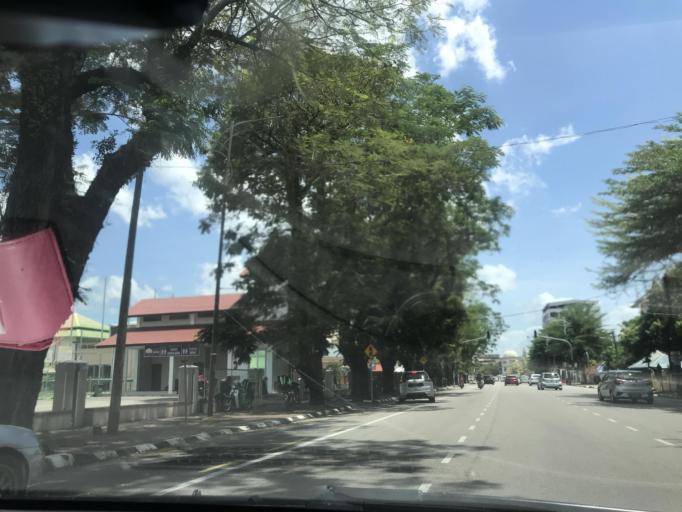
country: MY
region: Kelantan
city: Kota Bharu
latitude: 6.1251
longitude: 102.2416
